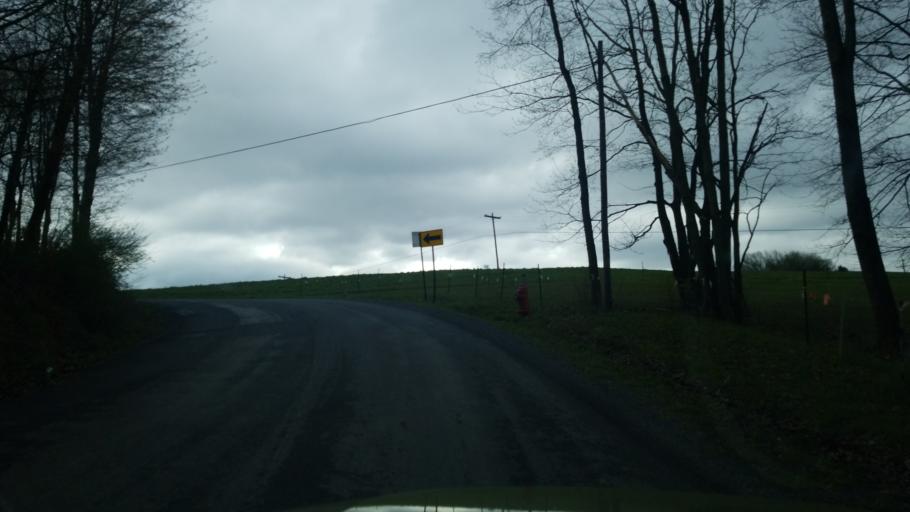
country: US
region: Pennsylvania
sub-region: Clearfield County
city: Clearfield
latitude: 41.0834
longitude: -78.4036
